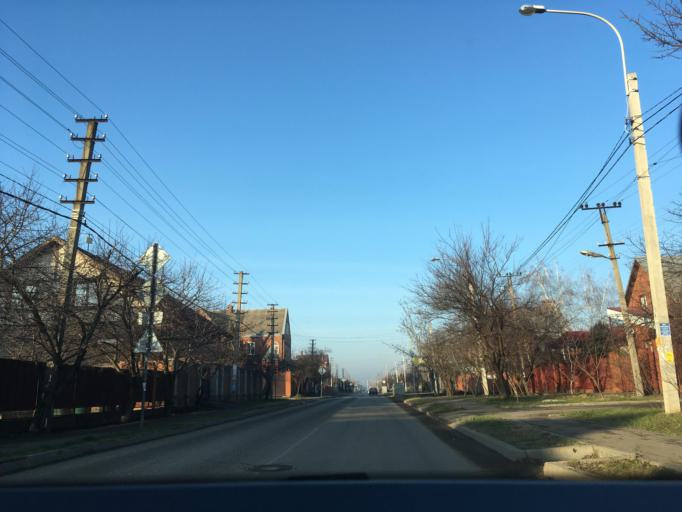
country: RU
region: Krasnodarskiy
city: Krasnodar
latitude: 45.1148
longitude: 39.0148
